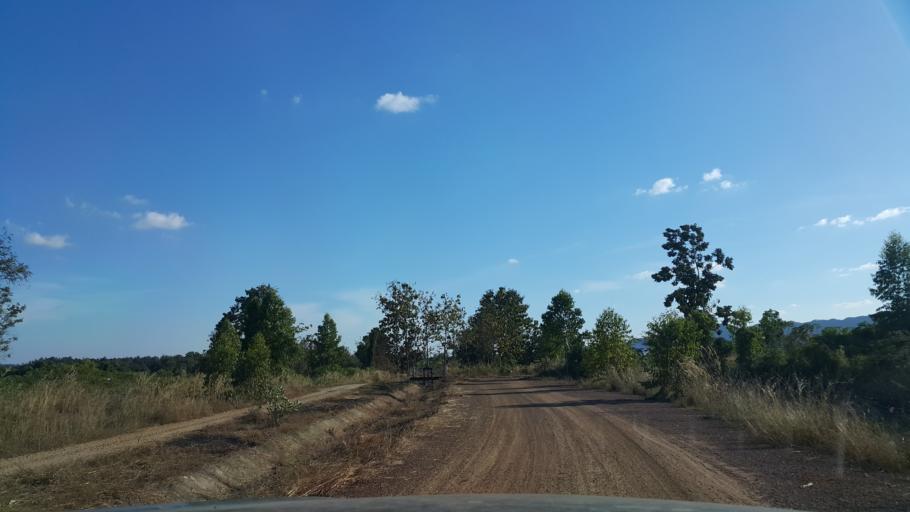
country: TH
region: Sukhothai
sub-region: Amphoe Si Satchanalai
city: Si Satchanalai
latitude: 17.4686
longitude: 99.6633
